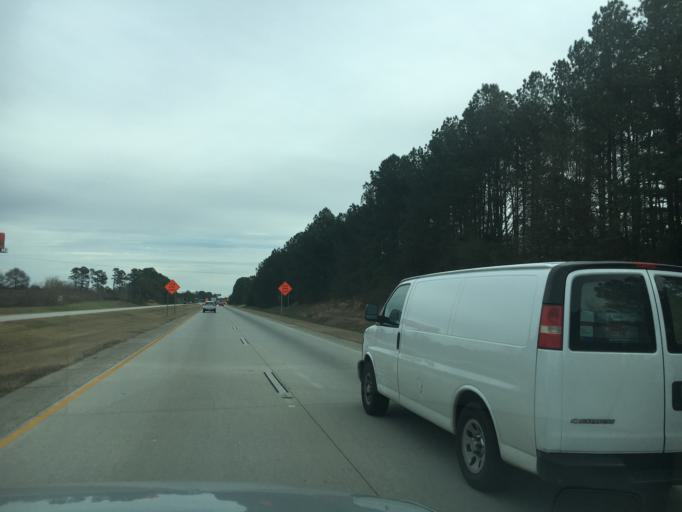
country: US
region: Georgia
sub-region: Barrow County
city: Winder
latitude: 33.9554
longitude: -83.7759
